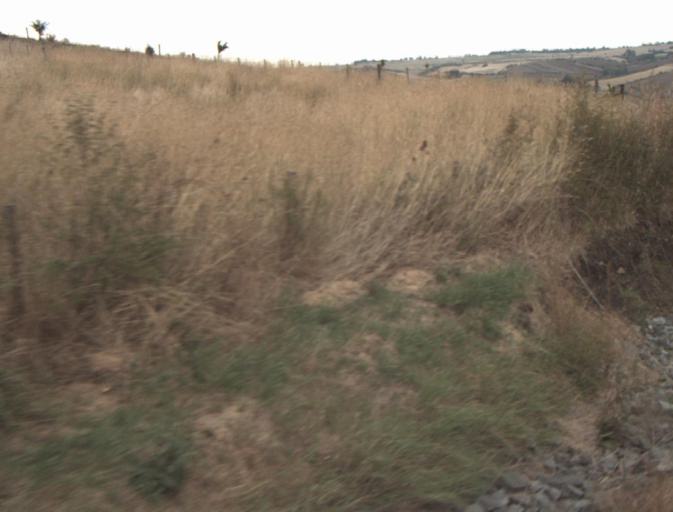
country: AU
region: Tasmania
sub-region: Northern Midlands
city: Evandale
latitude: -41.5245
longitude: 147.2472
